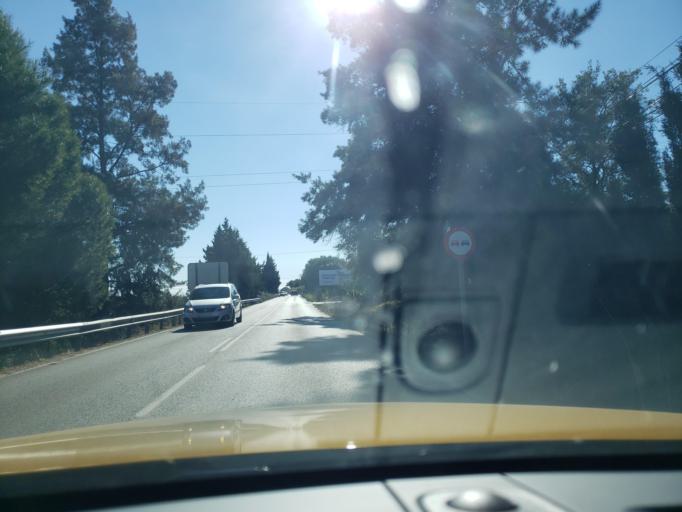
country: ES
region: Andalusia
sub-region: Provincia de Malaga
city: Benahavis
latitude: 36.4804
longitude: -5.0143
